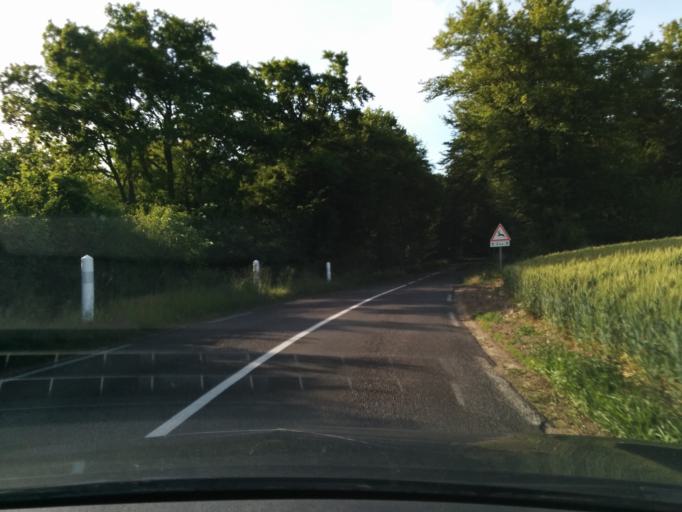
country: FR
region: Haute-Normandie
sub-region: Departement de l'Eure
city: Courcelles-sur-Seine
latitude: 49.1764
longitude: 1.3885
